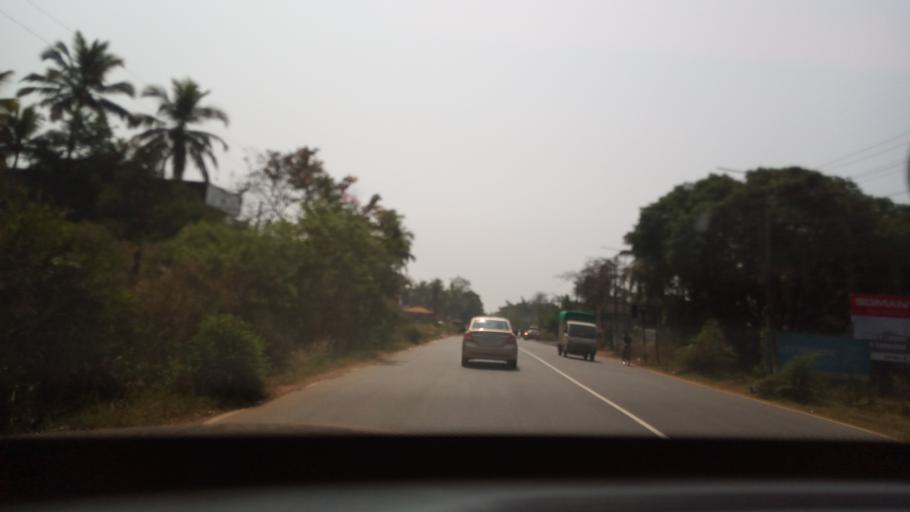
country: IN
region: Goa
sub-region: South Goa
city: Raia
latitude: 15.3202
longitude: 73.9414
